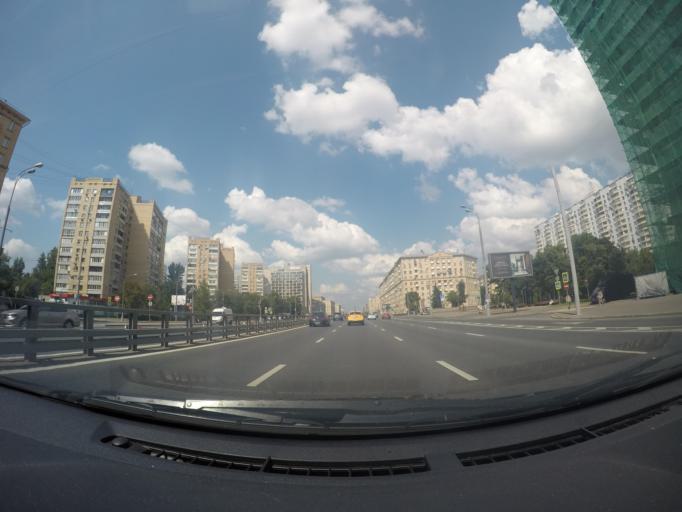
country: RU
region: Moscow
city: Mar'ina Roshcha
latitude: 55.8044
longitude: 37.6366
